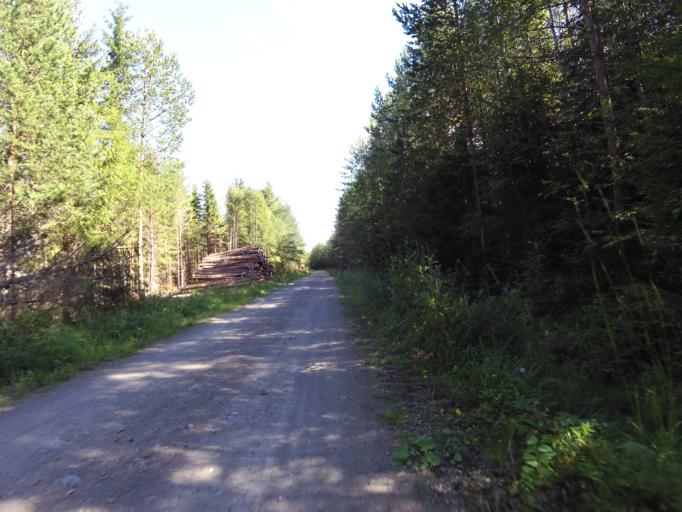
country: SE
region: Gaevleborg
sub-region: Hofors Kommun
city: Hofors
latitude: 60.5114
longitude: 16.3379
